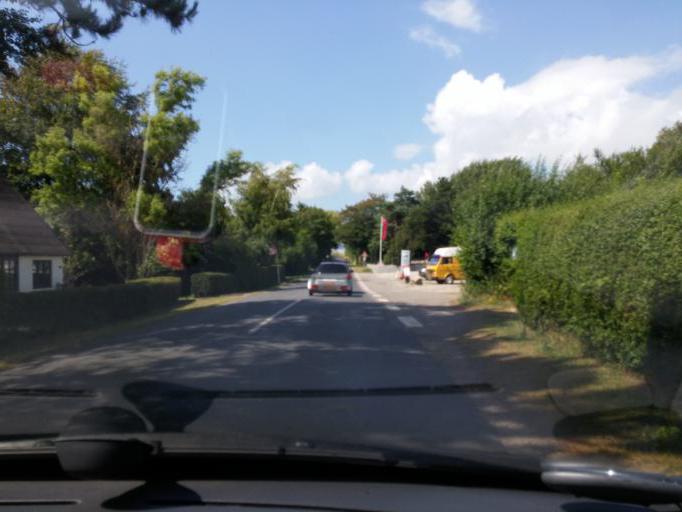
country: DK
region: South Denmark
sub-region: AEro Kommune
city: Marstal
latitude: 54.8192
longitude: 10.6402
